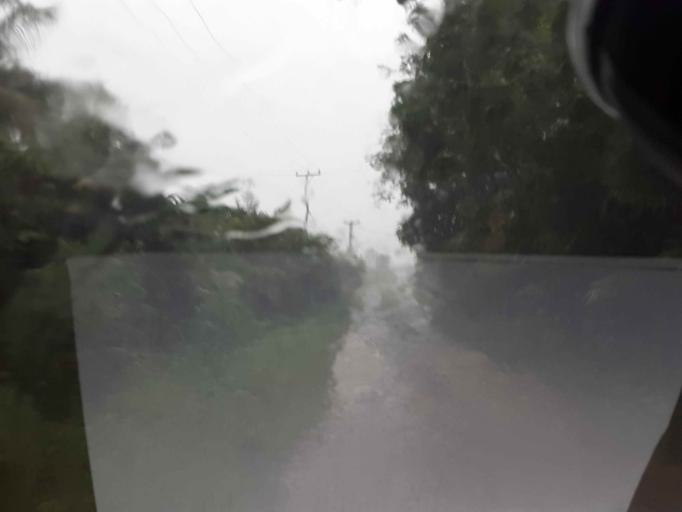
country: ID
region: Lampung
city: Kedaton
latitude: -5.3921
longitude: 105.3314
